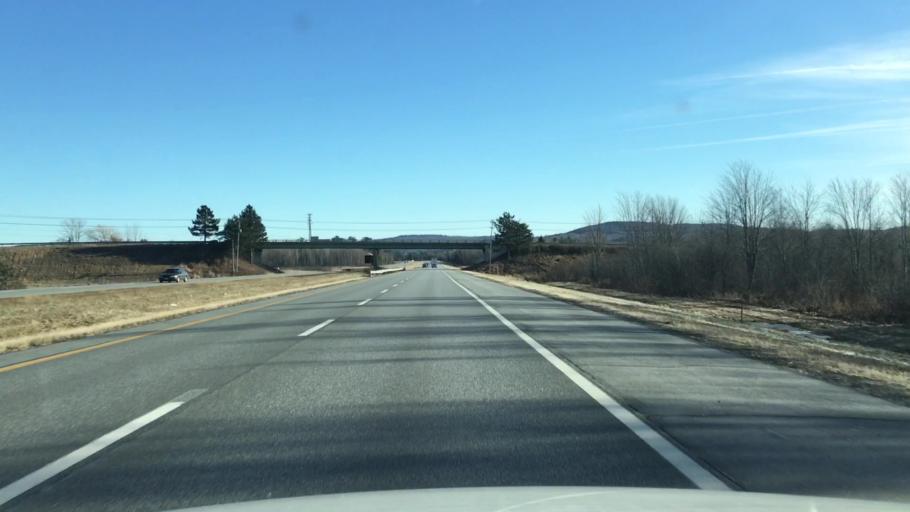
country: US
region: Maine
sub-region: Penobscot County
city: Brewer
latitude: 44.7750
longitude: -68.7484
